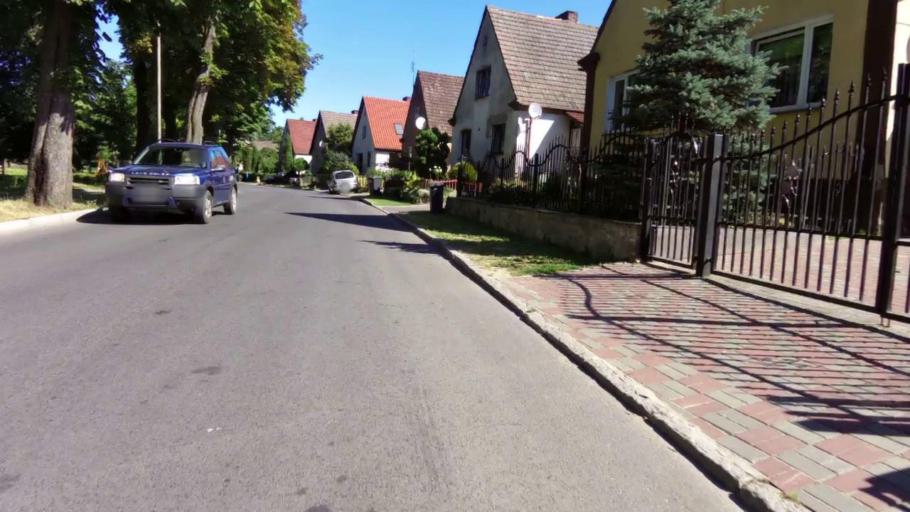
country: PL
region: West Pomeranian Voivodeship
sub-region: Powiat drawski
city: Zlocieniec
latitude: 53.5399
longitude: 16.0033
